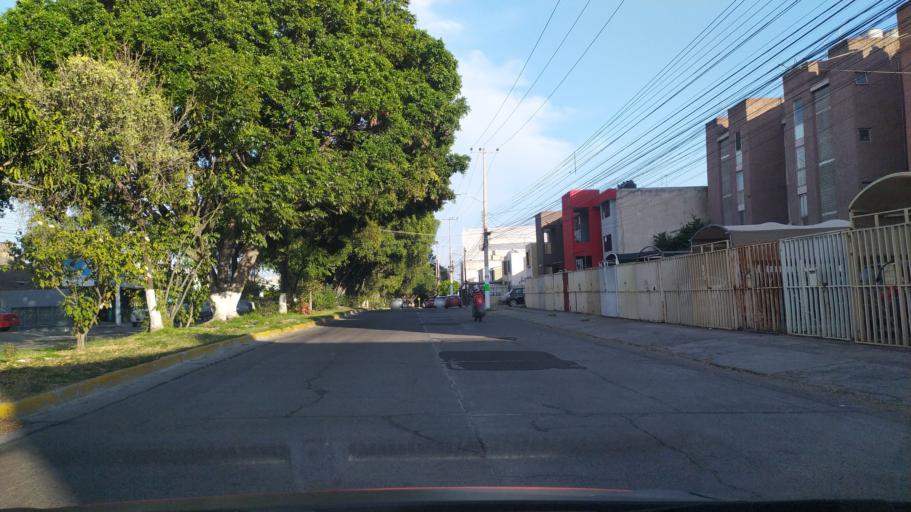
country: MX
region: Jalisco
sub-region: Tlajomulco de Zuniga
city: La Tijera
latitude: 20.6263
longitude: -103.4225
